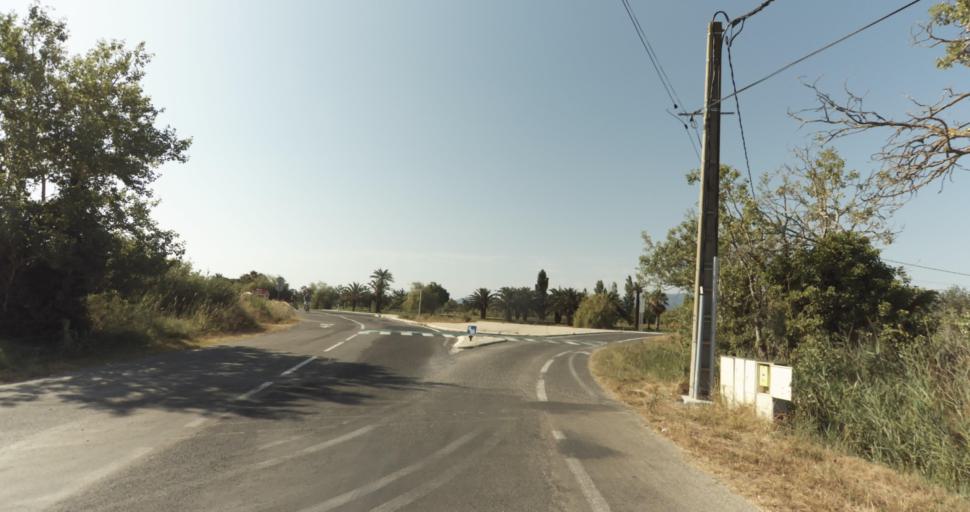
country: FR
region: Languedoc-Roussillon
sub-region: Departement des Pyrenees-Orientales
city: Saint-Cyprien-Plage
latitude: 42.6259
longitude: 3.0199
